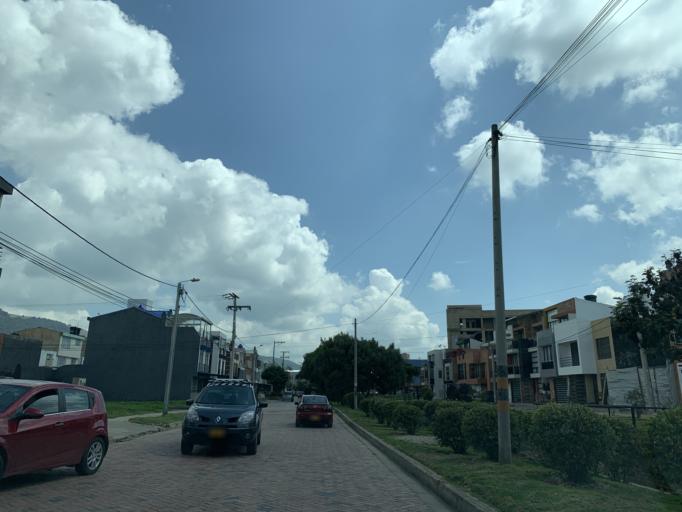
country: CO
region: Boyaca
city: Tunja
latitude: 5.5534
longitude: -73.3468
